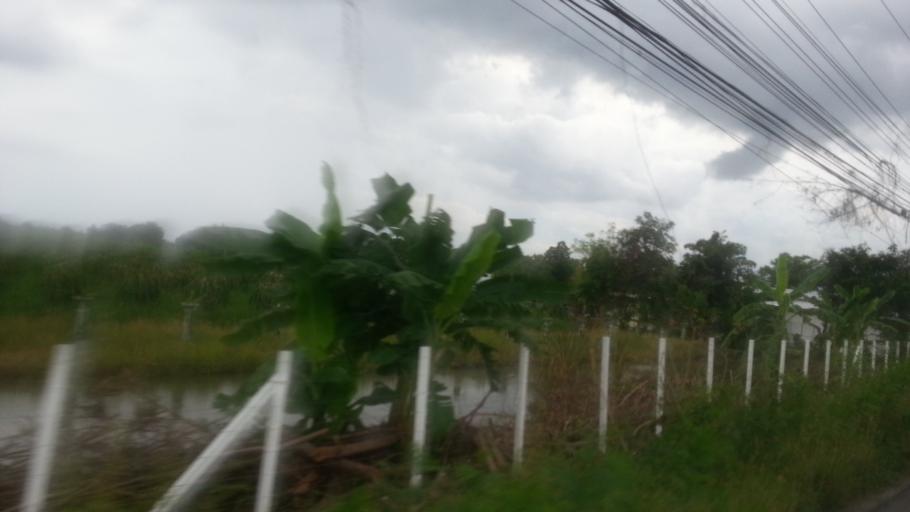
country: TH
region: Pathum Thani
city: Nong Suea
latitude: 14.0806
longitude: 100.8244
